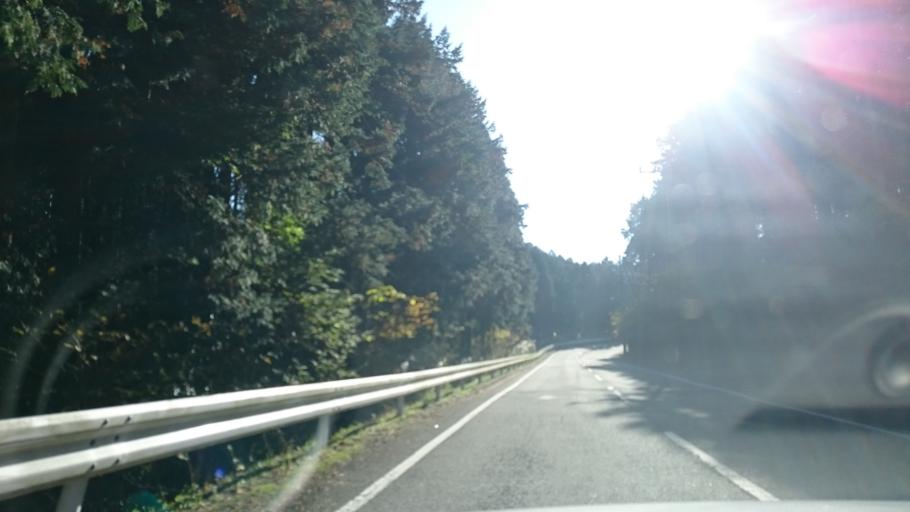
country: JP
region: Shizuoka
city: Heda
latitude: 34.9937
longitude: 138.8128
